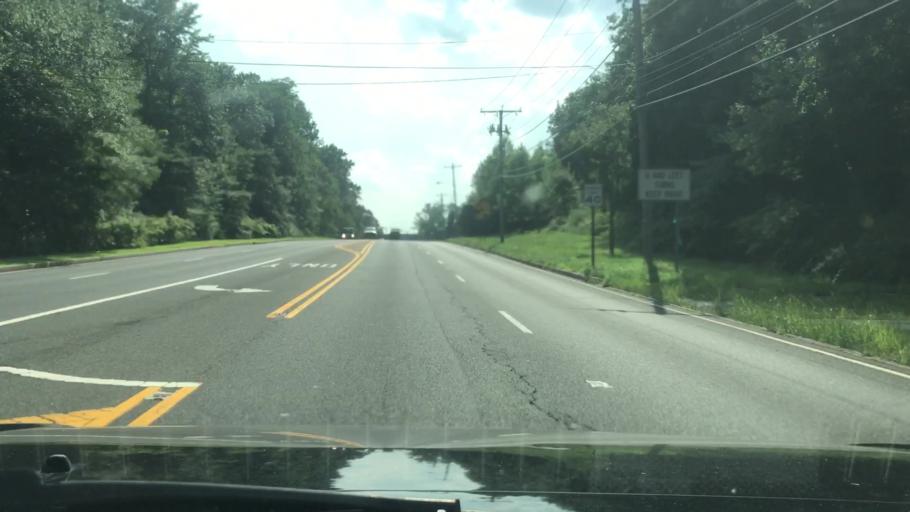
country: US
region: New Jersey
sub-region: Monmouth County
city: Eatontown
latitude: 40.2740
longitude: -74.0755
